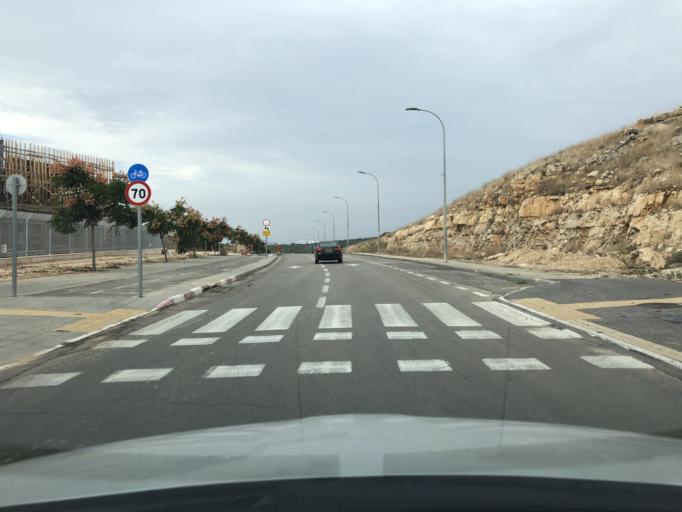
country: PS
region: West Bank
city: Al Midyah
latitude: 31.9184
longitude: 35.0017
